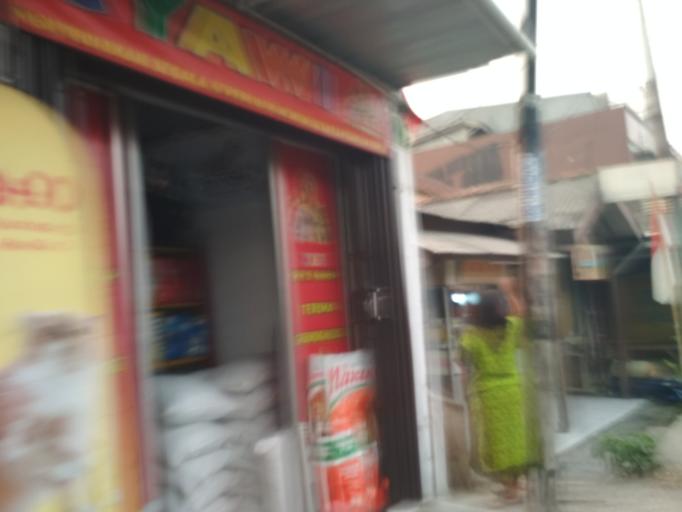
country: ID
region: West Java
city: Caringin
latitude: -6.6612
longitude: 106.8449
